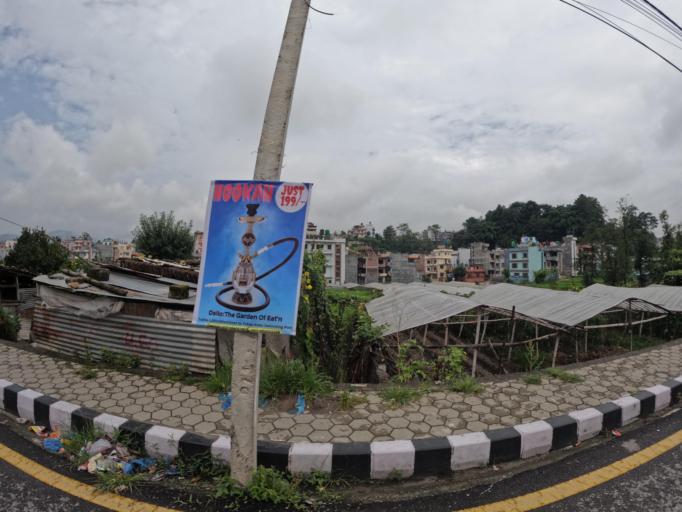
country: NP
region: Central Region
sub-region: Bagmati Zone
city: Kathmandu
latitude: 27.7580
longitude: 85.3252
